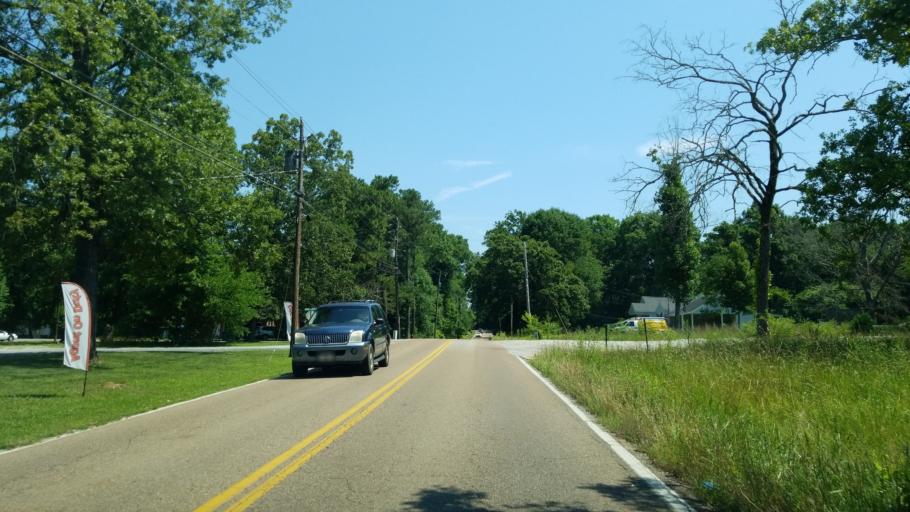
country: US
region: Tennessee
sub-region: Hamilton County
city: Collegedale
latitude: 35.0889
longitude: -85.0551
